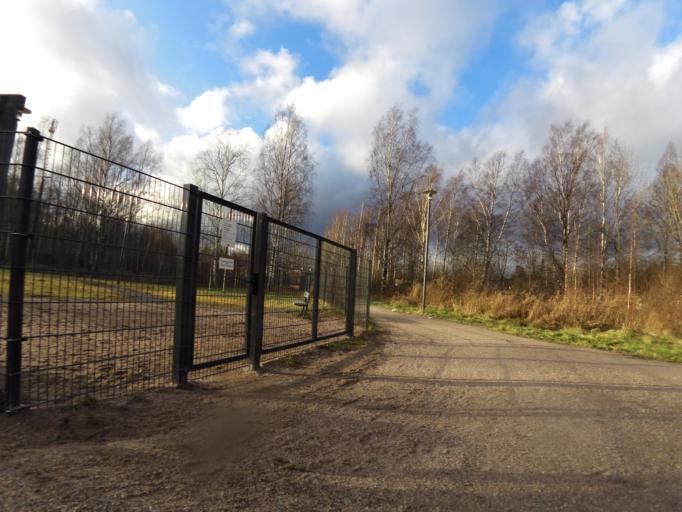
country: FI
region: Uusimaa
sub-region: Helsinki
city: Kilo
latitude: 60.1990
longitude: 24.7735
